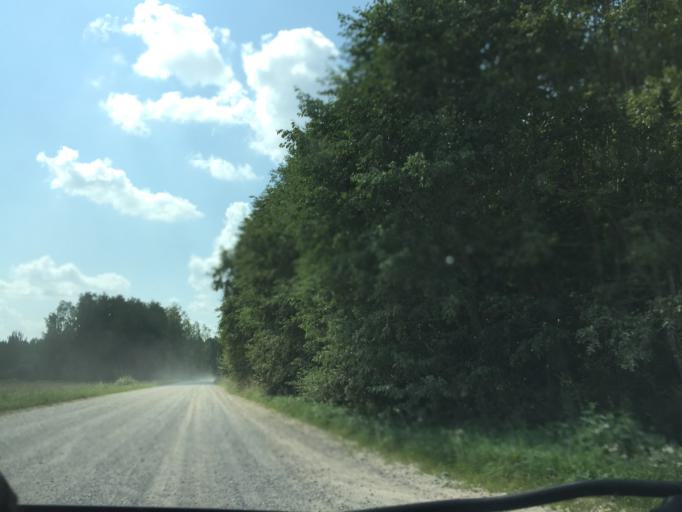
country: LV
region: Tervete
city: Zelmeni
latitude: 56.3984
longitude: 23.3216
